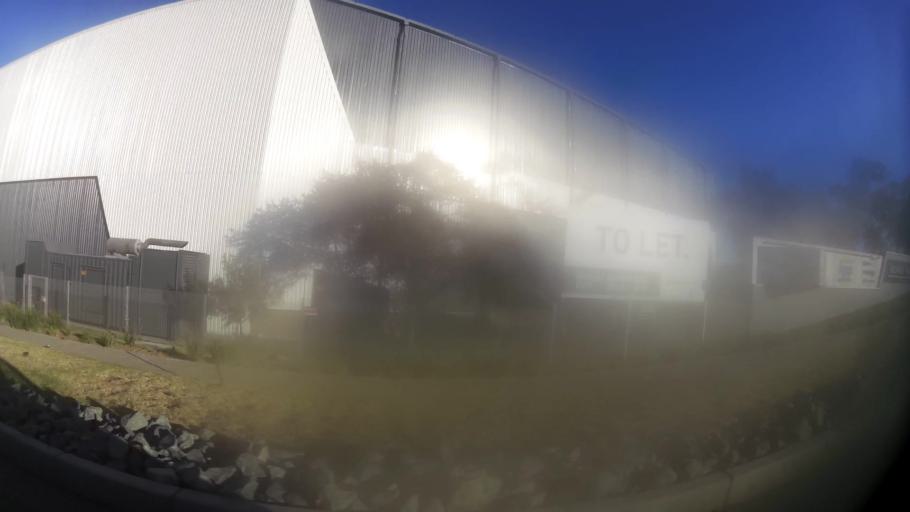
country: ZA
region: Gauteng
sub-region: City of Johannesburg Metropolitan Municipality
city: Midrand
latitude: -26.0135
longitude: 28.1193
